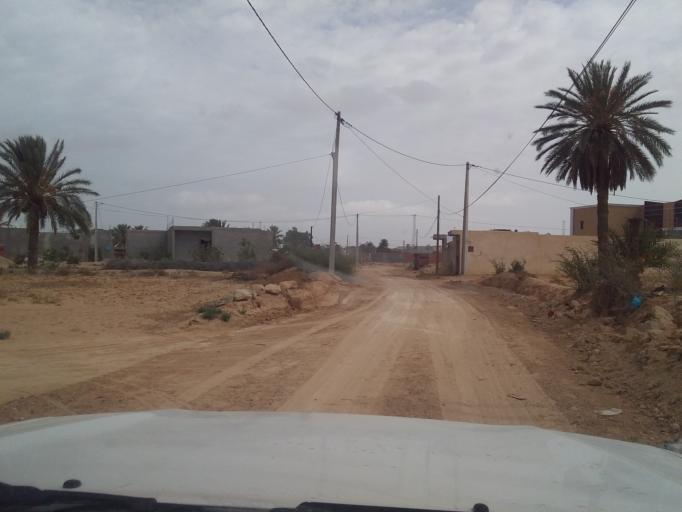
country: TN
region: Qabis
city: Matmata
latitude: 33.6204
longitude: 10.2656
